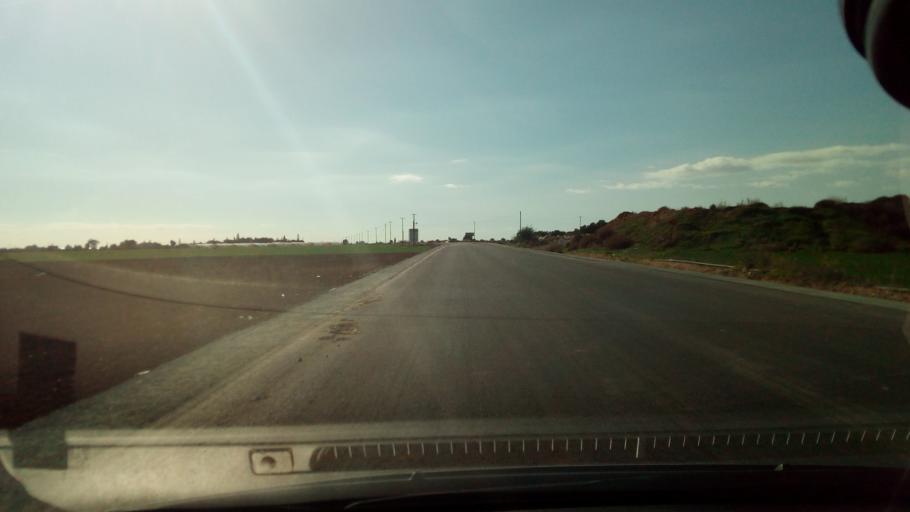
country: CY
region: Larnaka
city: Tersefanou
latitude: 34.8199
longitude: 33.5299
